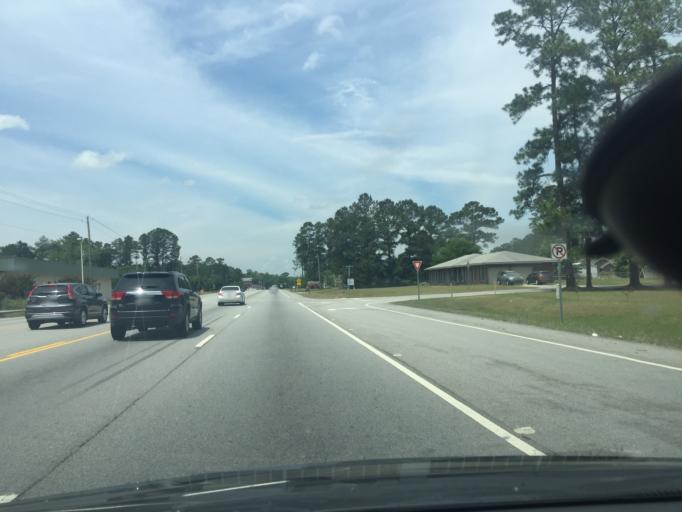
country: US
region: Georgia
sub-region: Chatham County
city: Bloomingdale
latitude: 32.1431
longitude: -81.3320
